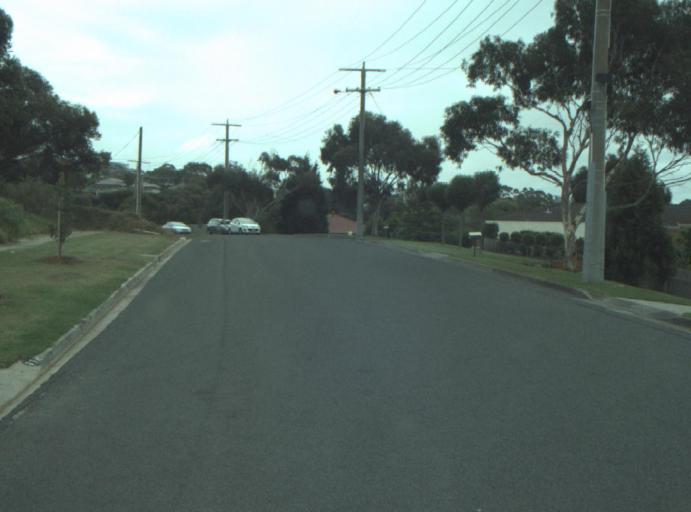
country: AU
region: Victoria
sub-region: Greater Geelong
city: Wandana Heights
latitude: -38.1814
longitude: 144.3049
